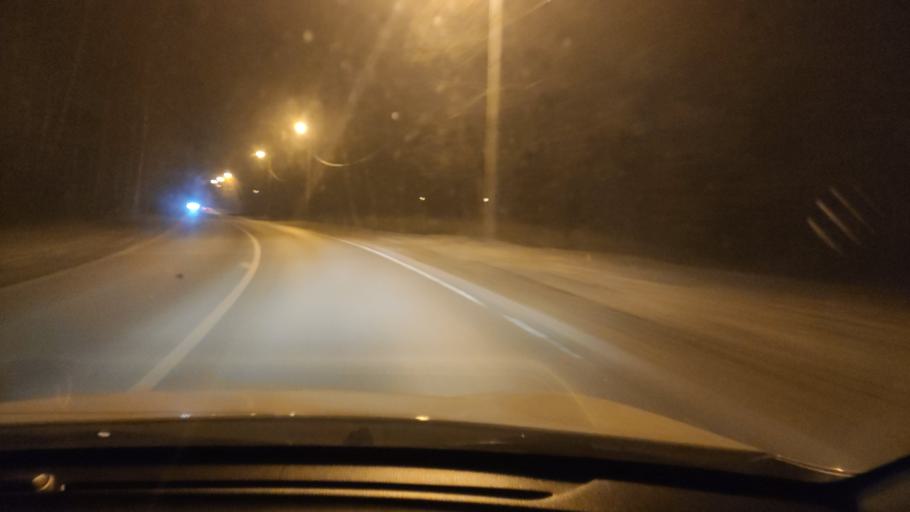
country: RU
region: Tatarstan
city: Osinovo
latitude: 55.8360
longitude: 48.8929
